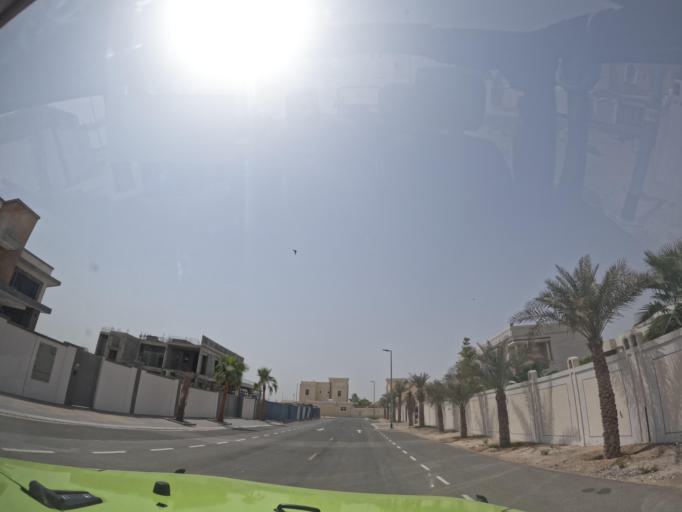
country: AE
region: Dubai
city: Dubai
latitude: 25.1325
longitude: 55.3614
